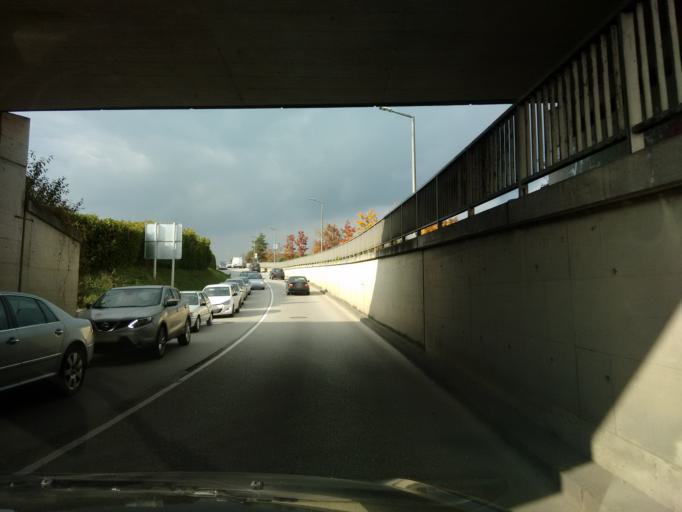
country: AT
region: Upper Austria
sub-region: Wels-Land
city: Gunskirchen
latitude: 48.1535
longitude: 13.9860
